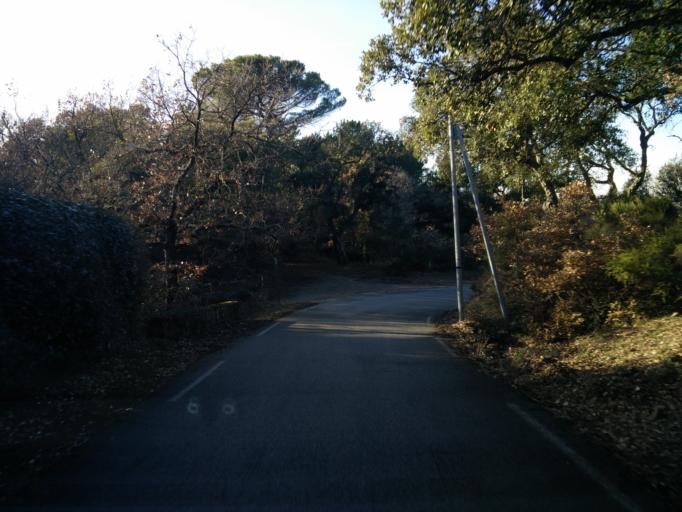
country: FR
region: Provence-Alpes-Cote d'Azur
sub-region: Departement du Var
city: La Garde-Freinet
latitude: 43.3393
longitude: 6.4762
